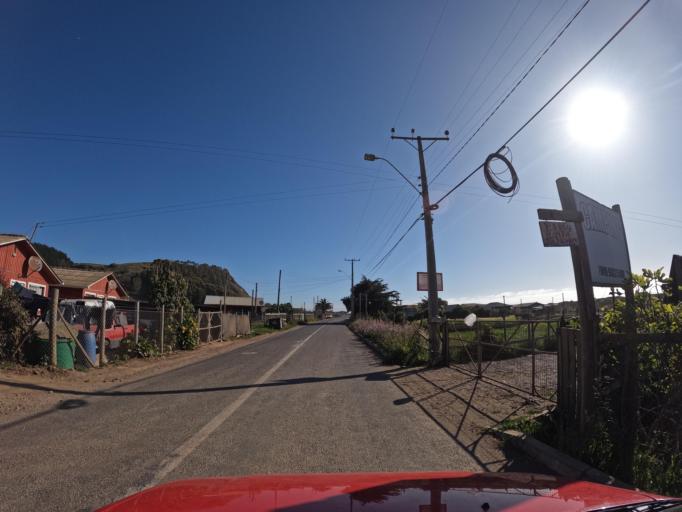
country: CL
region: Maule
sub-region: Provincia de Talca
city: Constitucion
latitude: -34.8544
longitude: -72.1431
